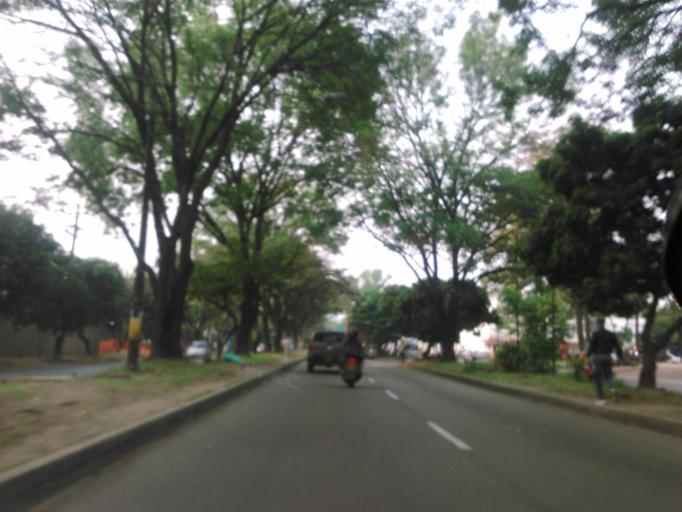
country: CO
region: Antioquia
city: Itagui
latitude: 6.1991
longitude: -75.5850
